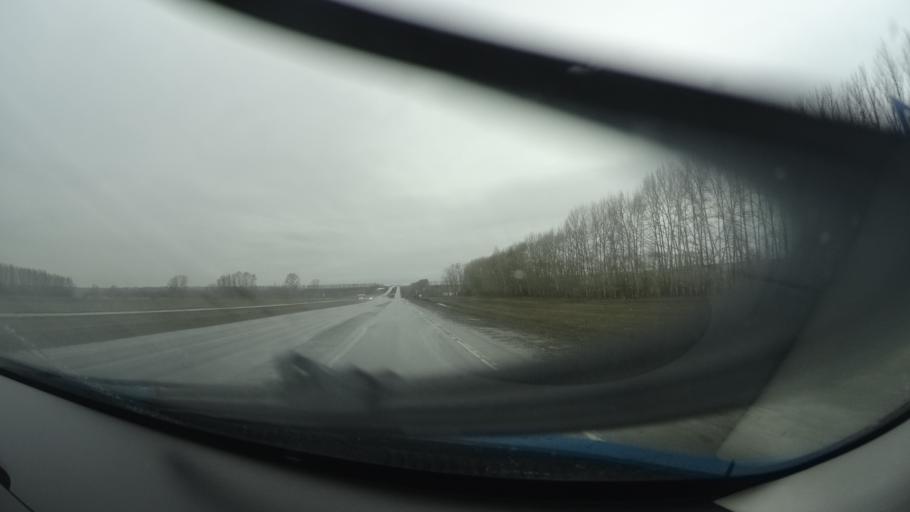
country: RU
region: Bashkortostan
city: Chishmy
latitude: 54.6628
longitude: 55.4384
